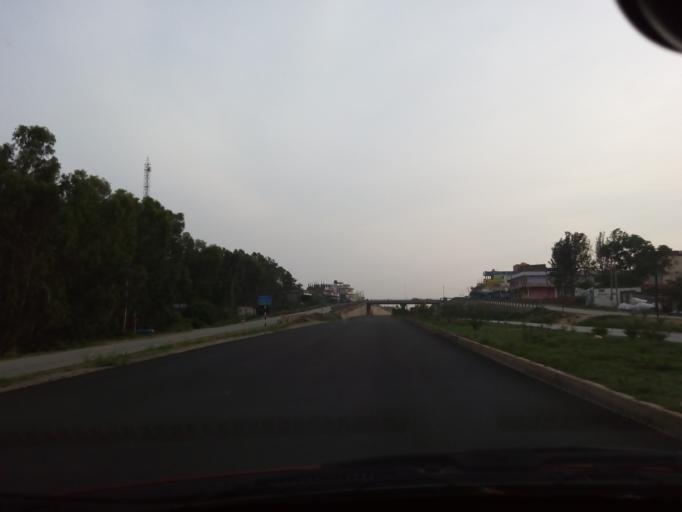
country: IN
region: Karnataka
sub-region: Chikkaballapur
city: Gudibanda
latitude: 13.5861
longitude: 77.7832
